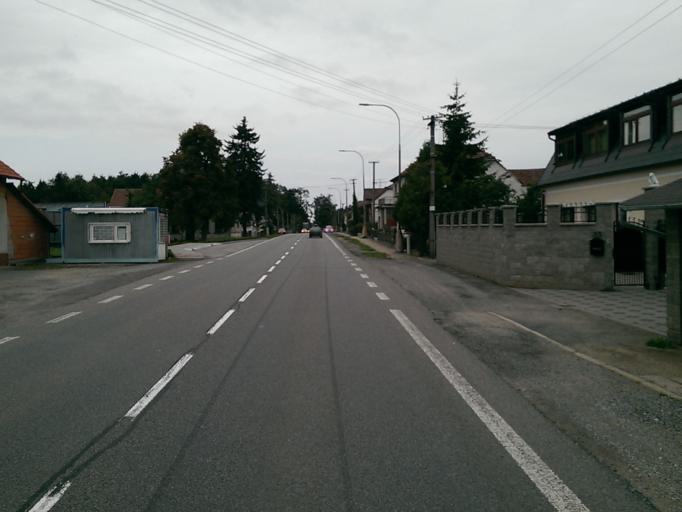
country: CZ
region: Vysocina
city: Zeletava
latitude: 49.1267
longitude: 15.6962
